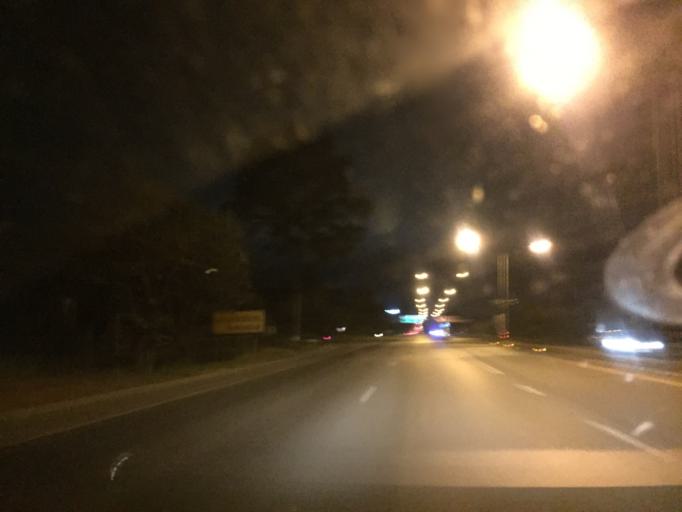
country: TH
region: Changwat Udon Thani
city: Udon Thani
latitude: 17.3617
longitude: 102.6977
